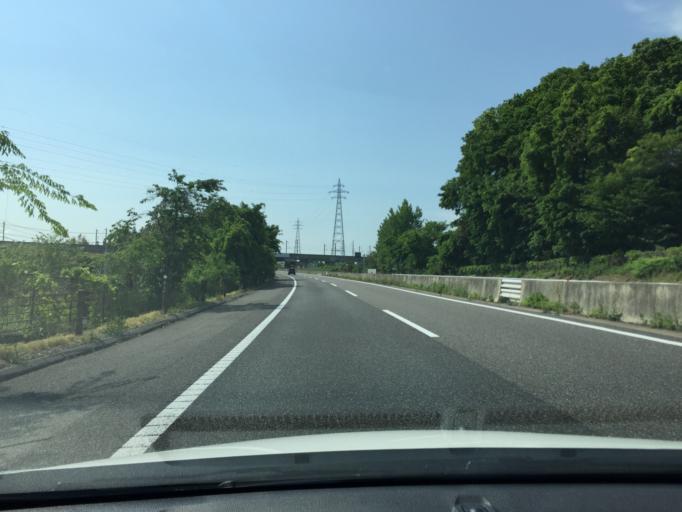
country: JP
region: Fukushima
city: Sukagawa
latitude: 37.3114
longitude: 140.3443
